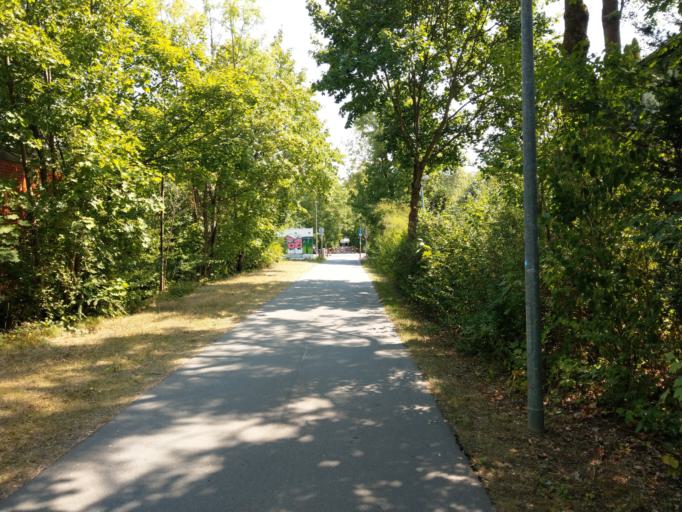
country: DE
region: Bavaria
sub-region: Upper Franconia
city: Bayreuth
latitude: 49.9306
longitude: 11.5697
